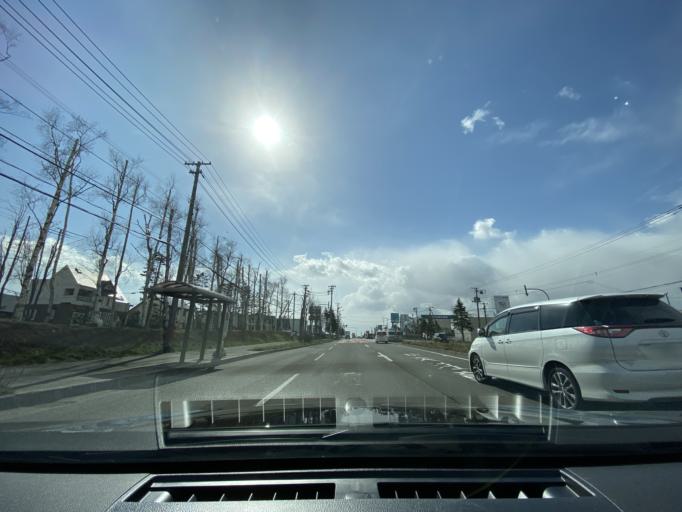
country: JP
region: Hokkaido
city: Kitahiroshima
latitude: 42.9643
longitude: 141.4876
